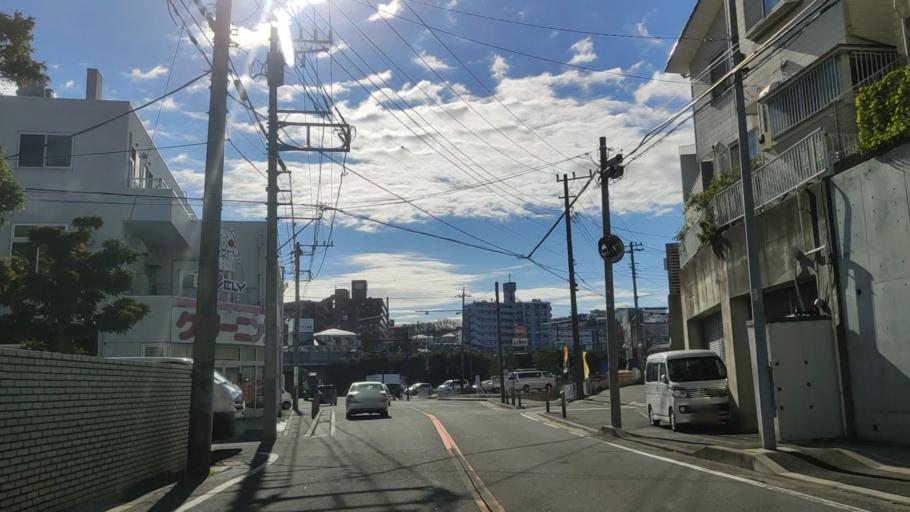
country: JP
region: Kanagawa
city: Yokohama
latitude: 35.4967
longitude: 139.6028
